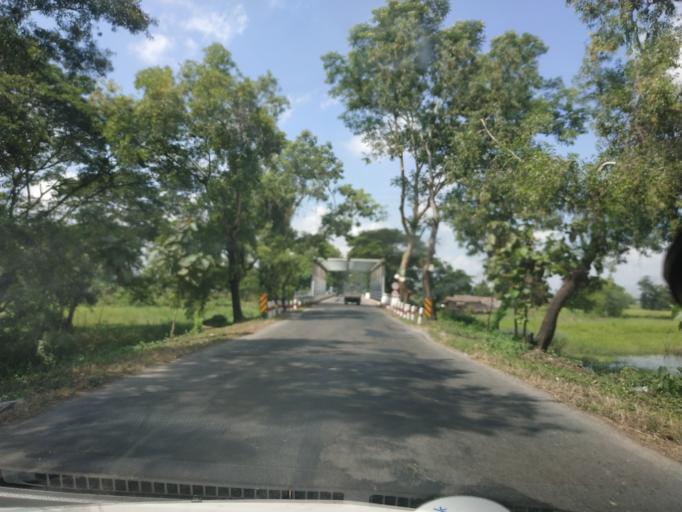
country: MM
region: Ayeyarwady
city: Nyaungdon
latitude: 17.0208
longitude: 95.4059
